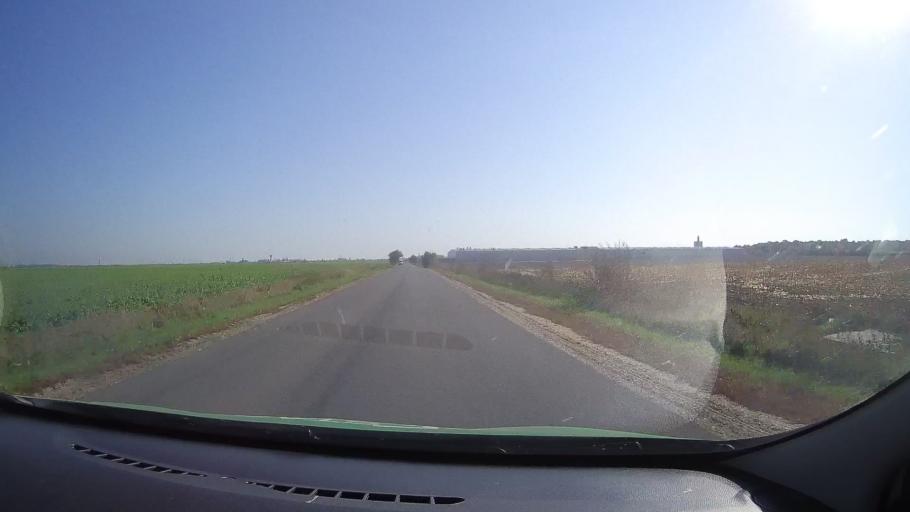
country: RO
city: Foieni
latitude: 47.6947
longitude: 22.4082
